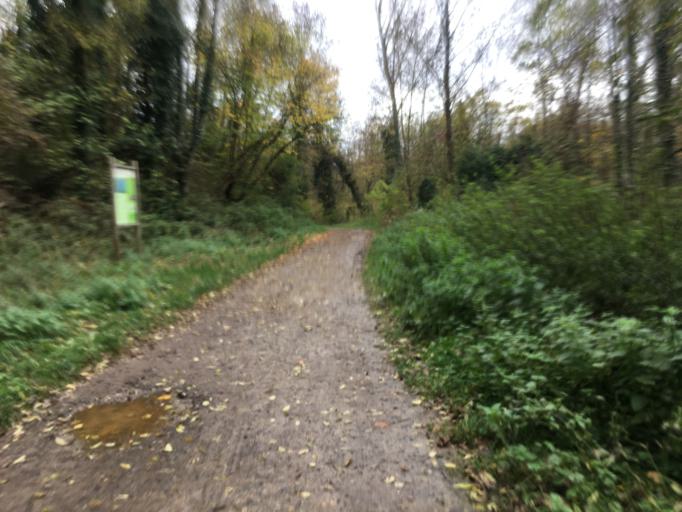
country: DE
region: Baden-Wuerttemberg
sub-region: Freiburg Region
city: Sasbach
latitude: 48.1070
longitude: 7.5892
